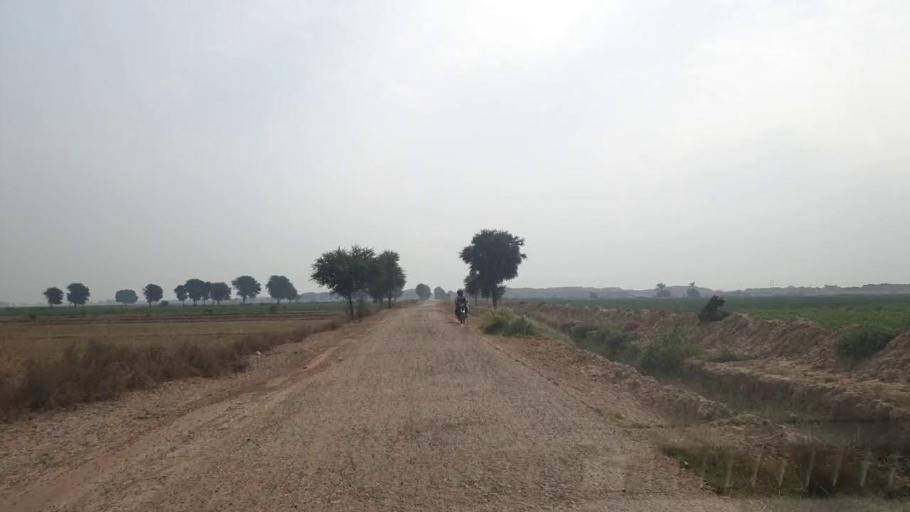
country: PK
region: Sindh
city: Sann
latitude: 26.0215
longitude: 68.1434
